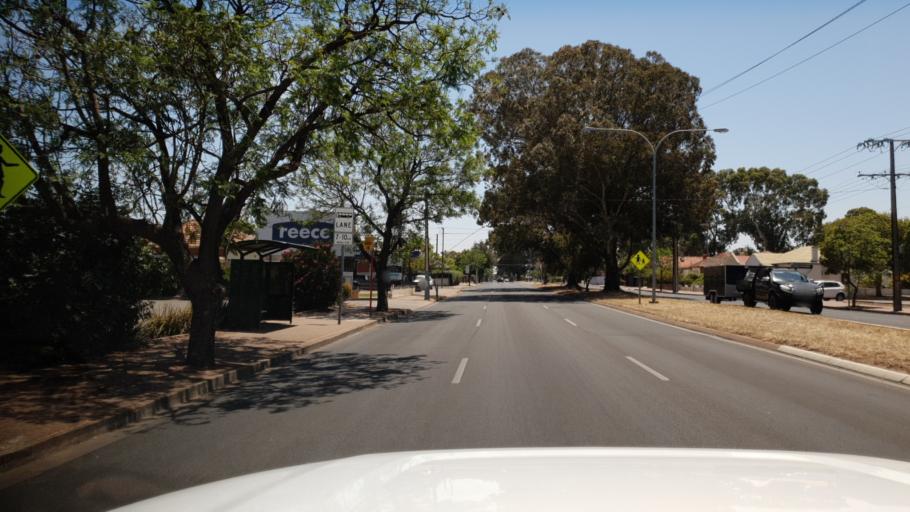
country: AU
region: South Australia
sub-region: Mitcham
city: Clapham
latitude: -34.9861
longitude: 138.5922
